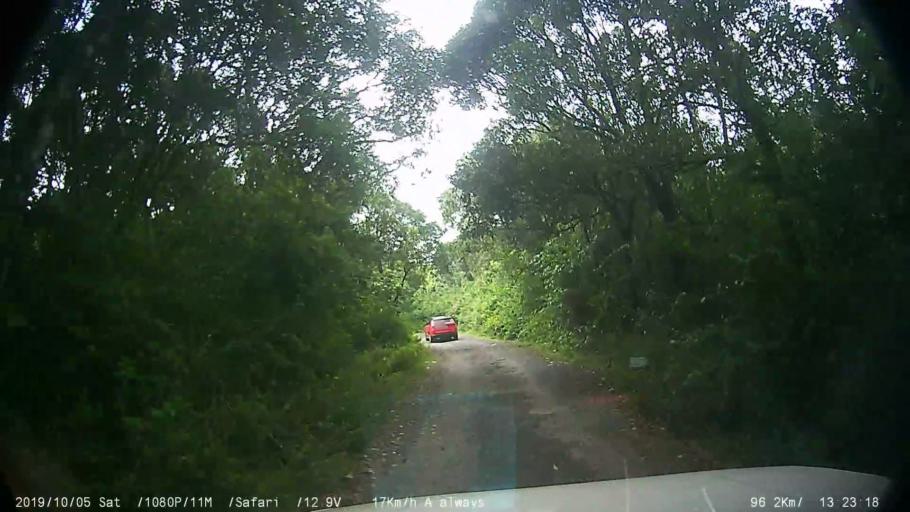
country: IN
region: Kerala
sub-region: Kottayam
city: Erattupetta
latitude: 9.5731
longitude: 76.9707
